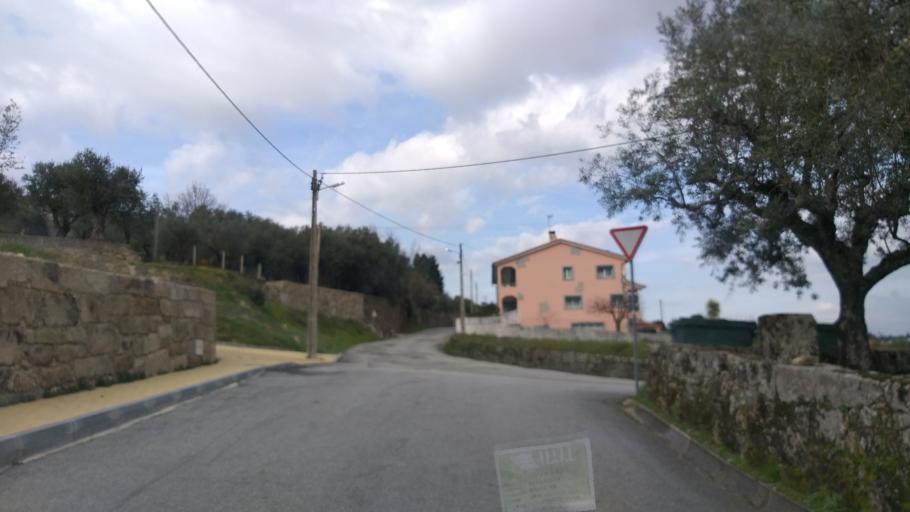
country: PT
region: Guarda
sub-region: Seia
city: Seia
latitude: 40.4638
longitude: -7.6891
